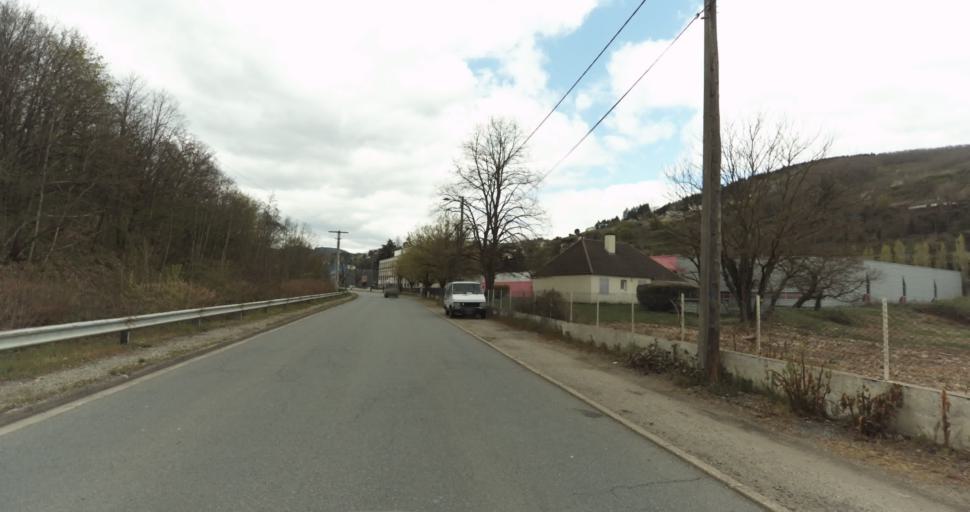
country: FR
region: Rhone-Alpes
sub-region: Departement du Rhone
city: Tarare
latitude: 45.8871
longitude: 4.4593
